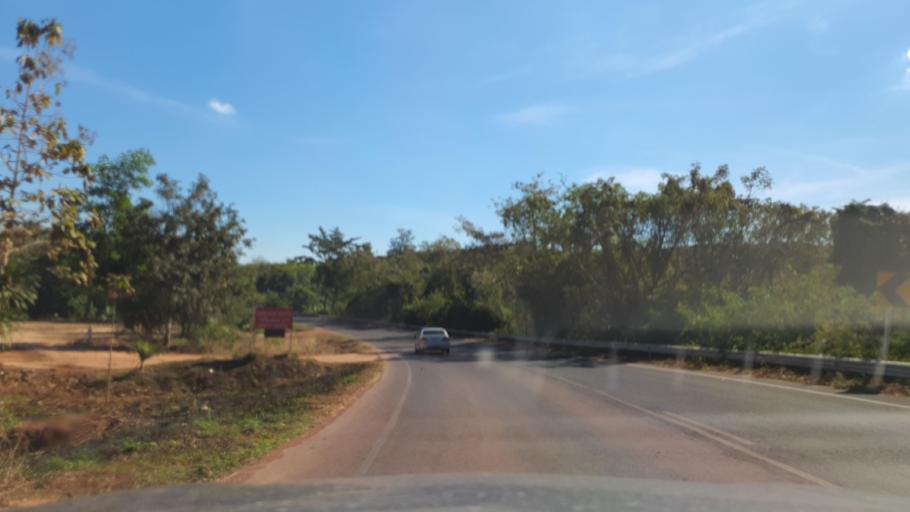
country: TH
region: Kalasin
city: Khao Wong
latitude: 16.7784
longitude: 104.1508
